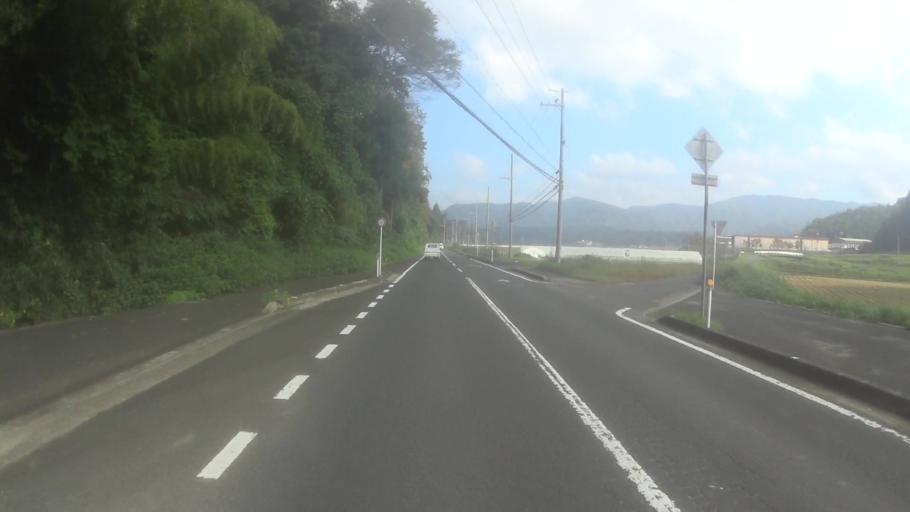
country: JP
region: Kyoto
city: Miyazu
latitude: 35.5852
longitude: 135.1318
